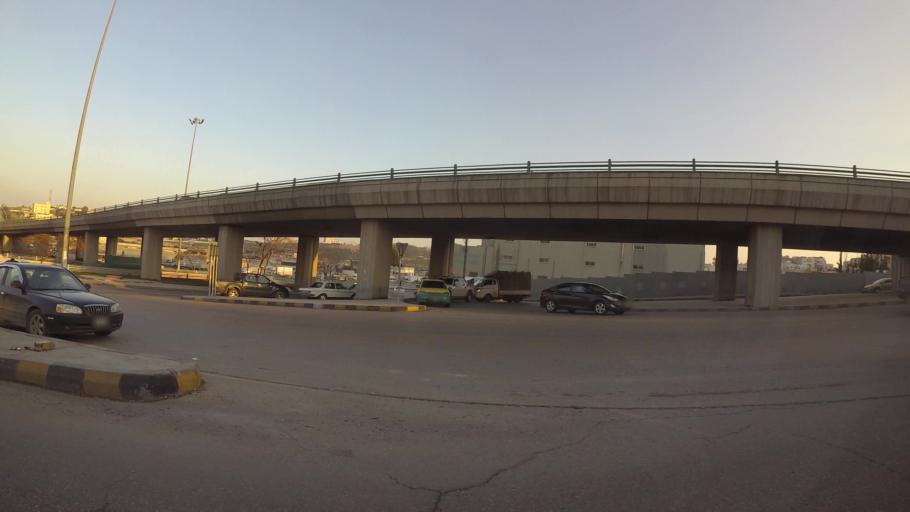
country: JO
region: Amman
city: Al Quwaysimah
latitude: 31.9010
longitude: 35.9375
